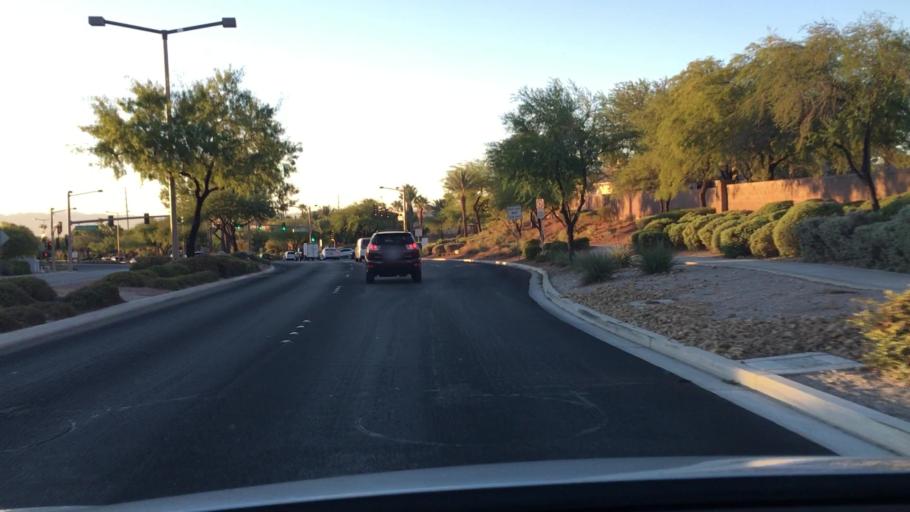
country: US
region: Nevada
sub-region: Clark County
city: Summerlin South
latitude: 36.1467
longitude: -115.3418
